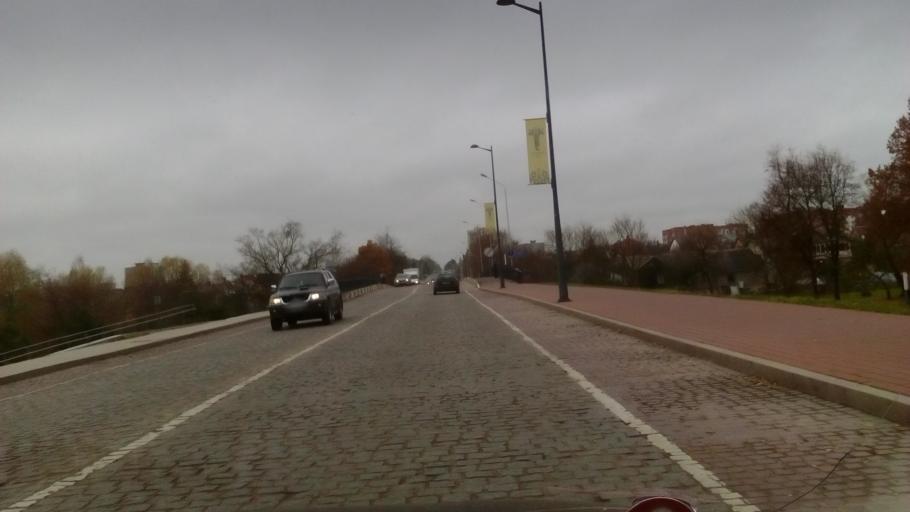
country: LT
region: Marijampoles apskritis
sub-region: Marijampole Municipality
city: Marijampole
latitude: 54.5589
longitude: 23.3467
